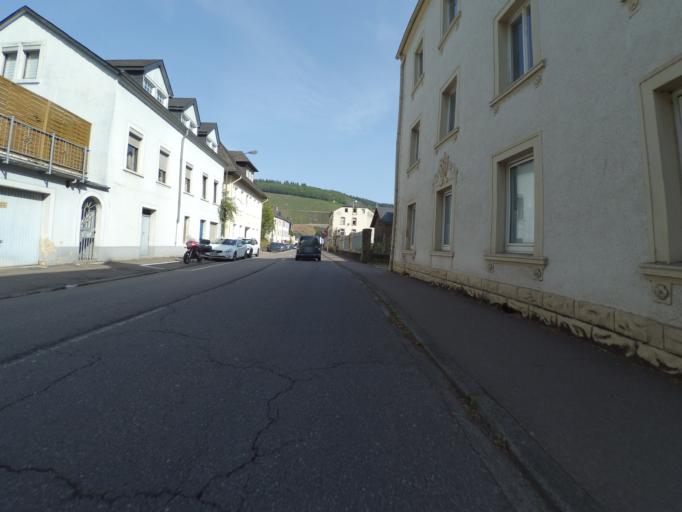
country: DE
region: Rheinland-Pfalz
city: Saarburg
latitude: 49.6099
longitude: 6.5537
